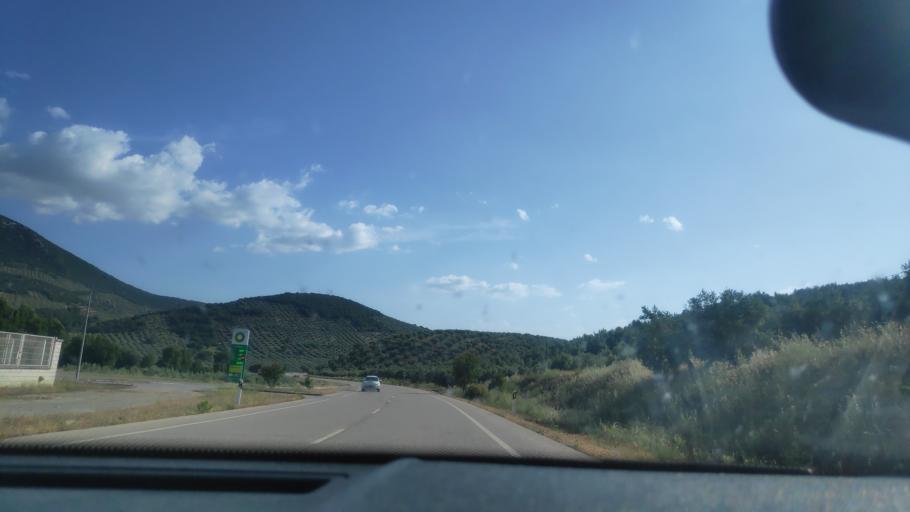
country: ES
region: Andalusia
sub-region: Provincia de Granada
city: Benalua de las Villas
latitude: 37.4445
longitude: -3.6507
